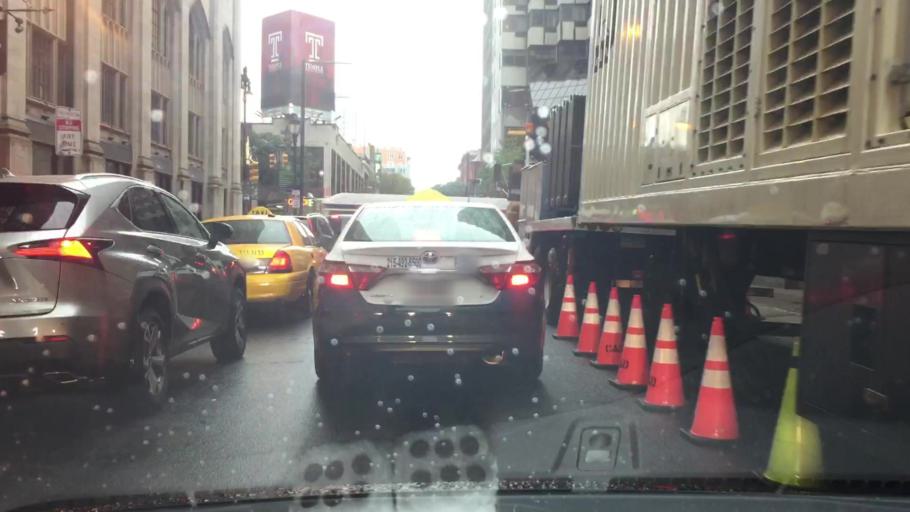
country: US
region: Pennsylvania
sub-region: Philadelphia County
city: Philadelphia
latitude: 39.9484
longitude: -75.1652
